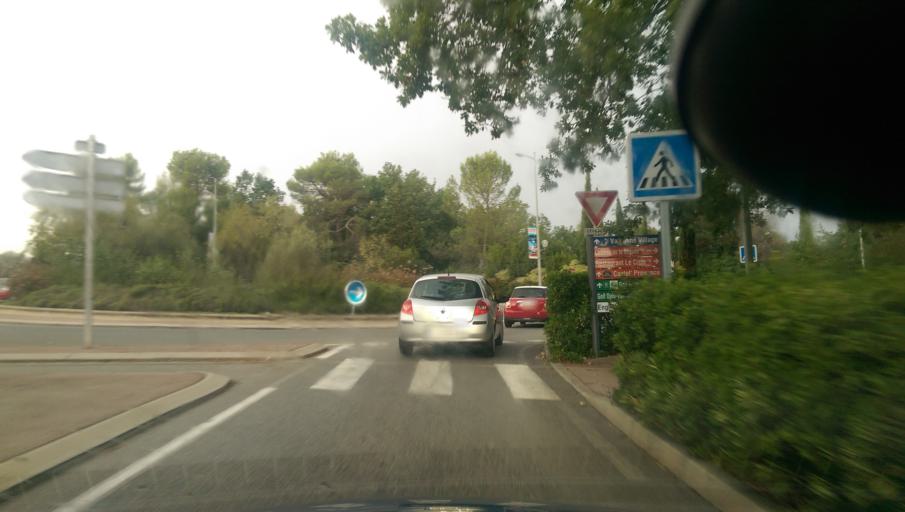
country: FR
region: Provence-Alpes-Cote d'Azur
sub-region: Departement des Alpes-Maritimes
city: Valbonne
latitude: 43.6440
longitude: 7.0207
